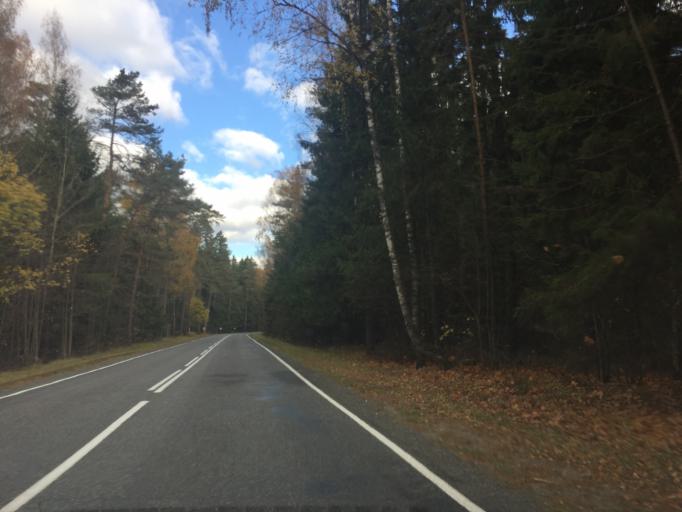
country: BY
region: Minsk
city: Narach
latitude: 54.9362
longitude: 26.5642
